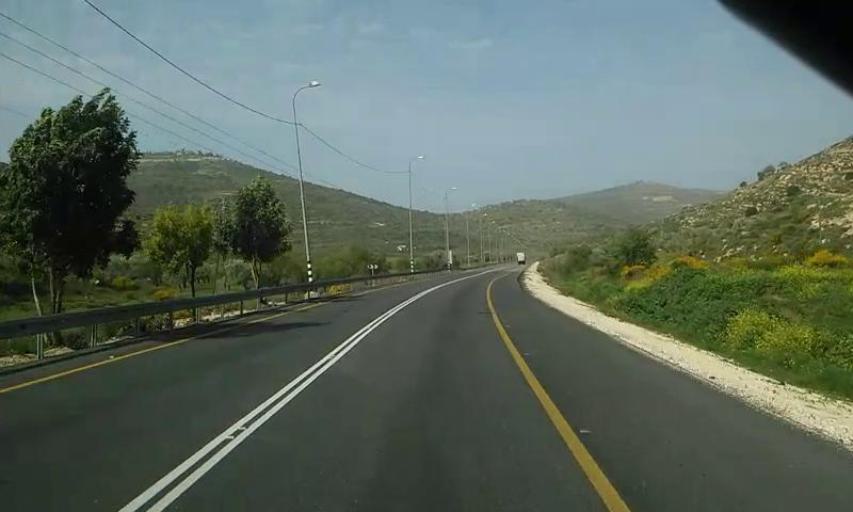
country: PS
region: West Bank
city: Al Lubban ash Sharqiyah
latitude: 32.0625
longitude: 35.2531
